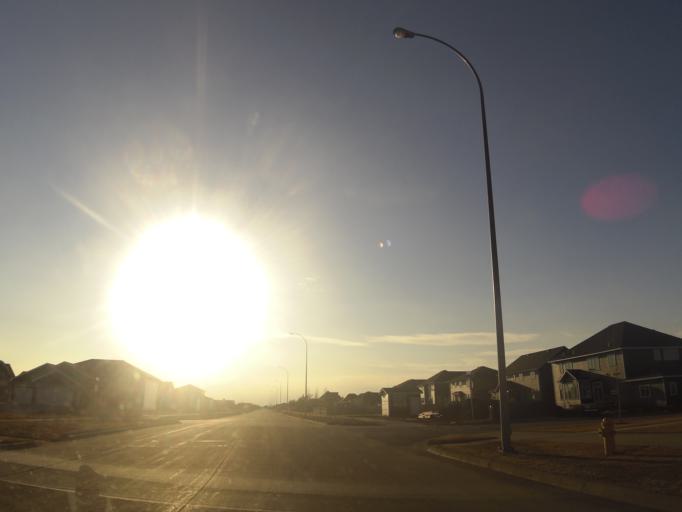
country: US
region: North Dakota
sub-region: Grand Forks County
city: Grand Forks
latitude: 47.8676
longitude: -97.0323
